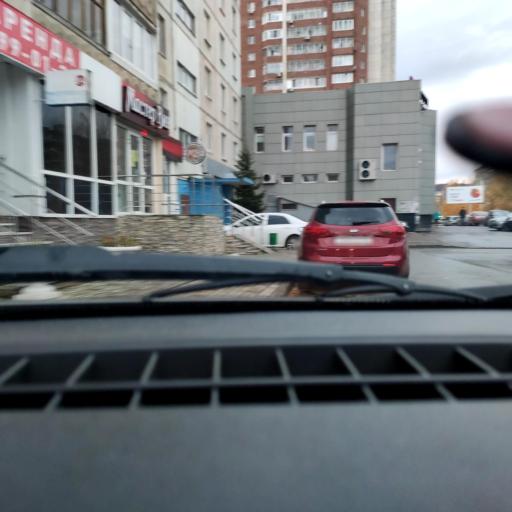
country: RU
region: Bashkortostan
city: Ufa
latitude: 54.7641
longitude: 56.0636
